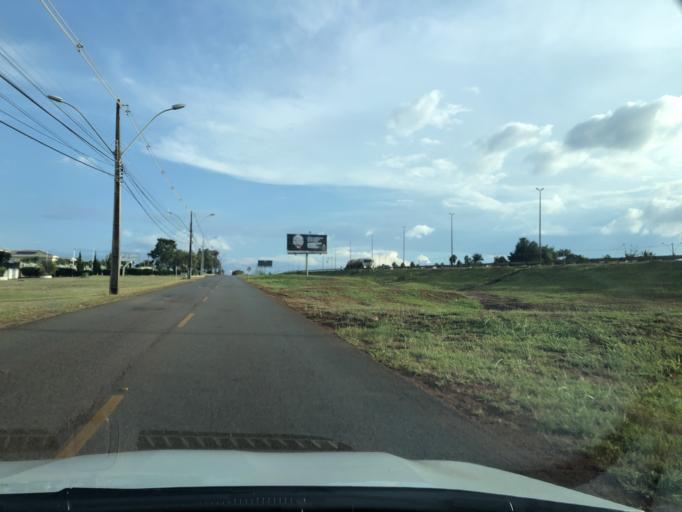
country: BR
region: Federal District
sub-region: Brasilia
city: Brasilia
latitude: -15.8949
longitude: -47.9615
